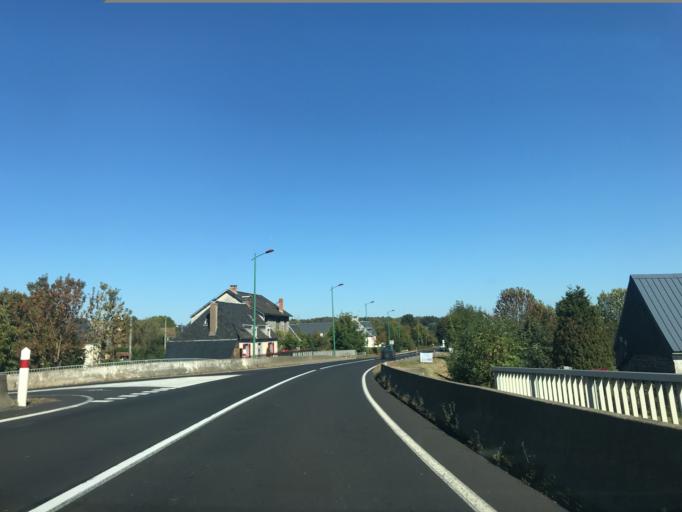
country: FR
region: Auvergne
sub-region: Departement du Puy-de-Dome
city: Gelles
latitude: 45.7233
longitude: 2.8013
